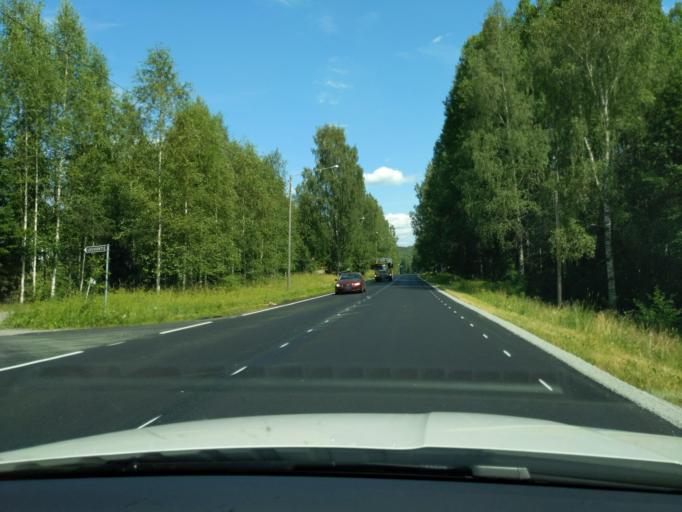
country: FI
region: Paijanne Tavastia
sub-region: Lahti
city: Lahti
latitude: 61.0669
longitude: 25.8089
